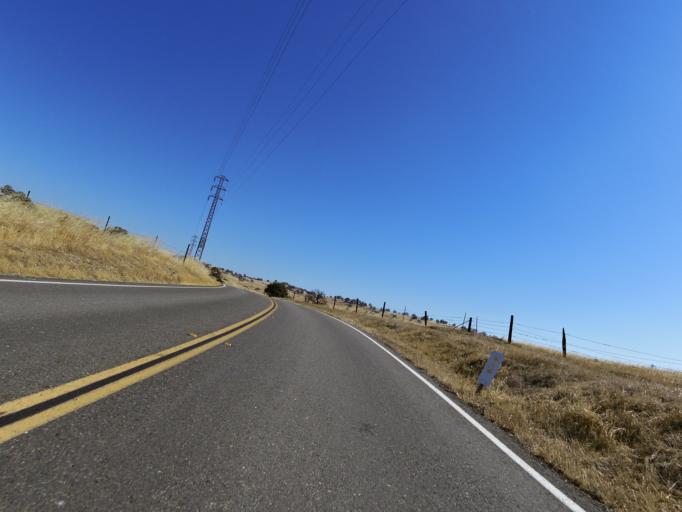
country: US
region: California
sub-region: Merced County
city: Planada
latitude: 37.5331
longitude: -120.3280
